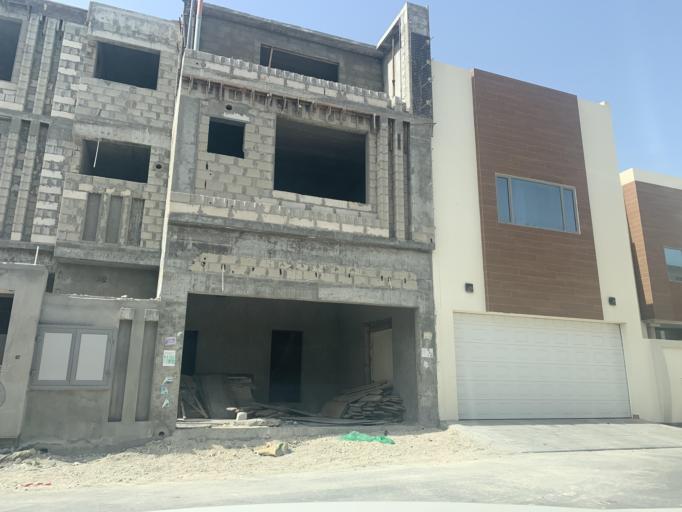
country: BH
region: Northern
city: Sitrah
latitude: 26.1667
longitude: 50.6291
